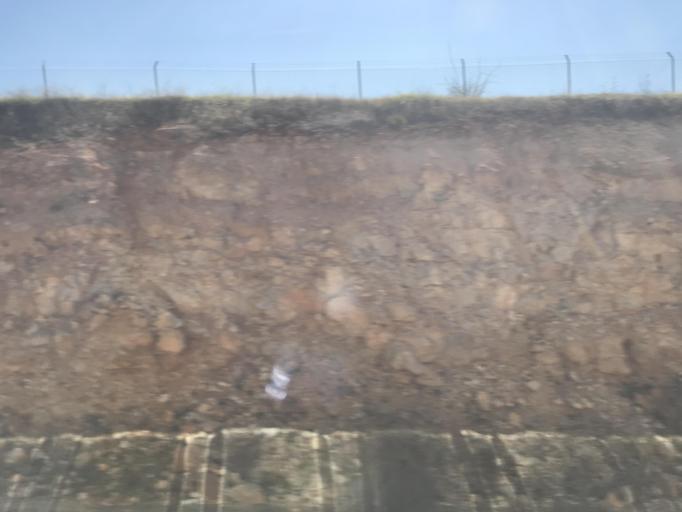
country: ES
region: Castille-La Mancha
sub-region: Provincia de Guadalajara
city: Alaminos
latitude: 40.8915
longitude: -2.7179
